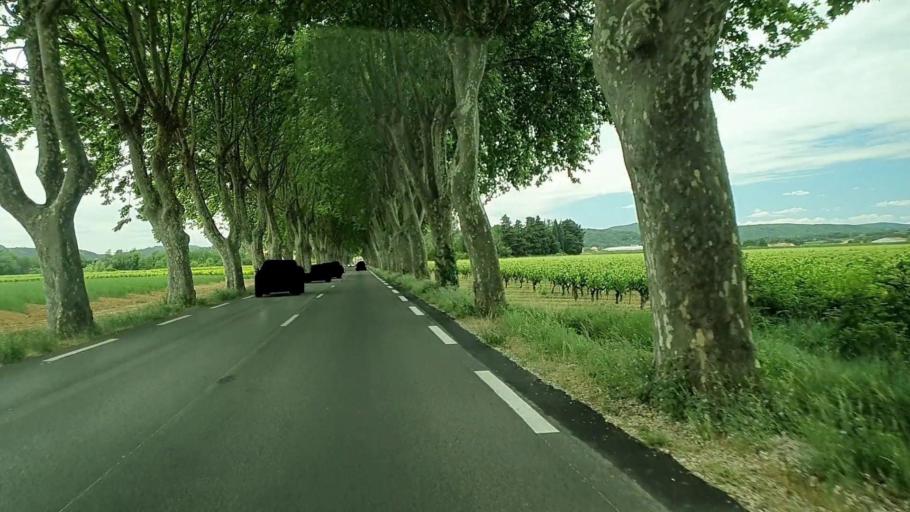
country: FR
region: Languedoc-Roussillon
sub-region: Departement du Gard
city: Connaux
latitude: 44.0991
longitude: 4.6028
